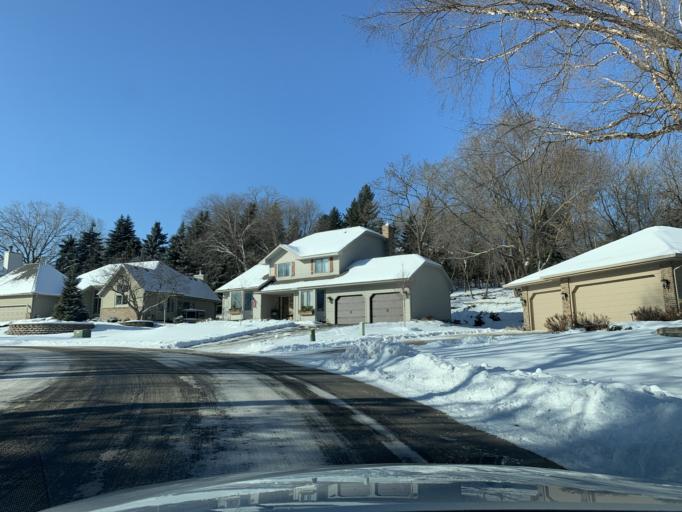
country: US
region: Minnesota
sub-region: Hennepin County
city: Bloomington
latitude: 44.8357
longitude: -93.3451
